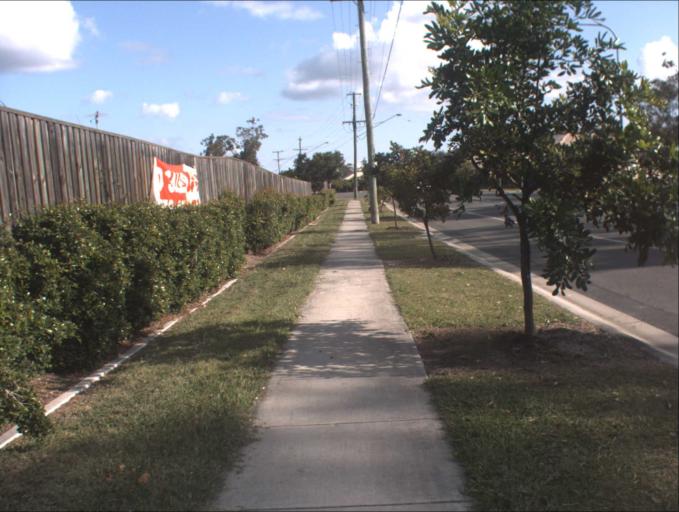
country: AU
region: Queensland
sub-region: Logan
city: Park Ridge South
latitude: -27.6843
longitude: 153.0501
